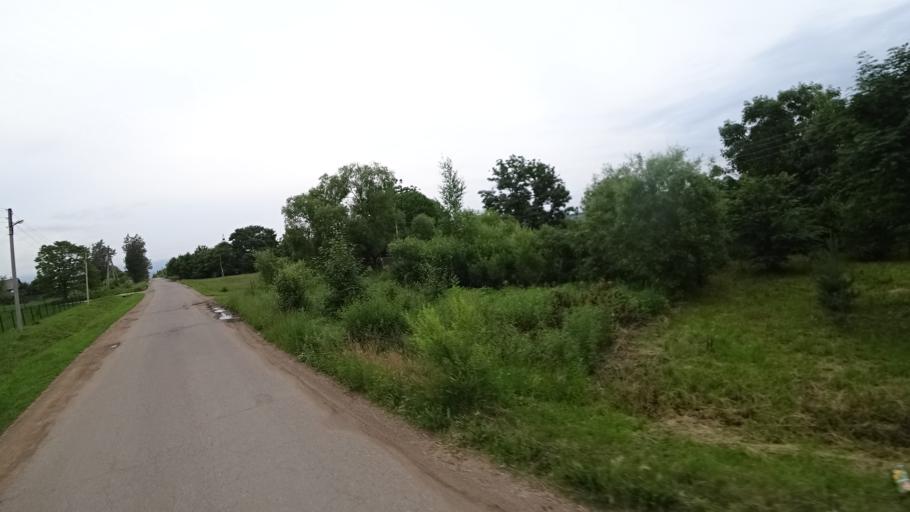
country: RU
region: Primorskiy
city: Novosysoyevka
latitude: 44.2298
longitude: 133.3609
